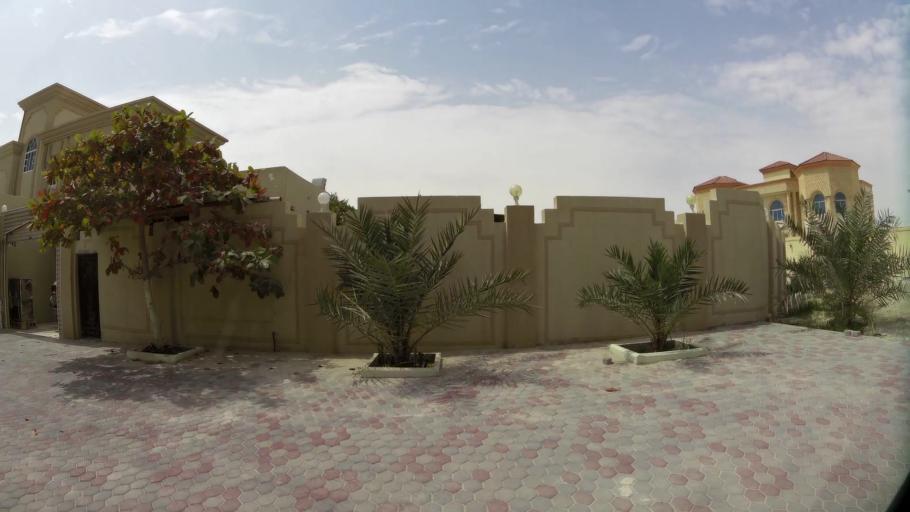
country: QA
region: Baladiyat ar Rayyan
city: Ar Rayyan
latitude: 25.3562
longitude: 51.4734
